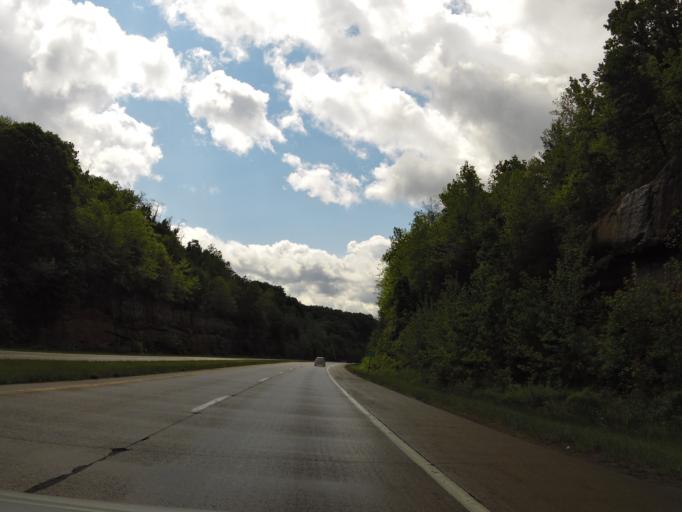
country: US
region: Ohio
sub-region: Athens County
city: Athens
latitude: 39.3489
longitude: -82.0843
